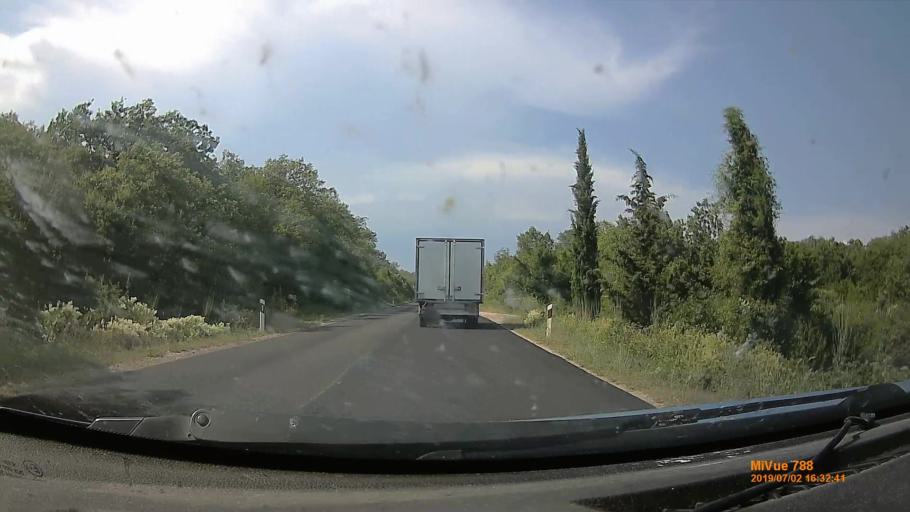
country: HR
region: Primorsko-Goranska
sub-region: Grad Krk
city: Krk
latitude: 45.0674
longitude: 14.4882
